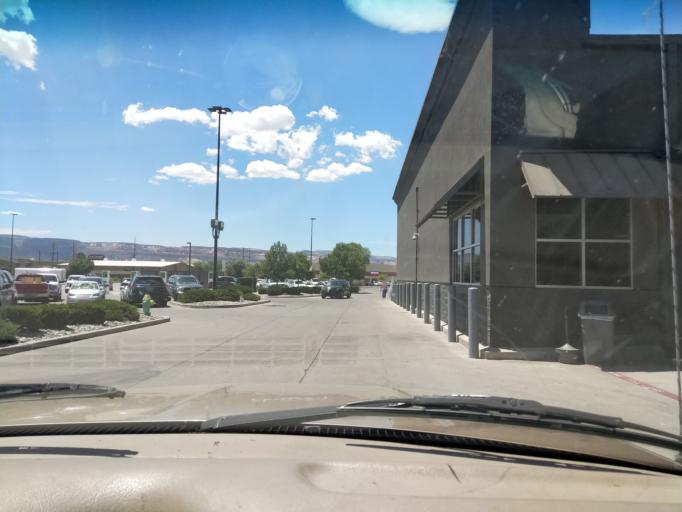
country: US
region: Colorado
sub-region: Mesa County
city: Grand Junction
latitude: 39.0745
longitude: -108.5736
